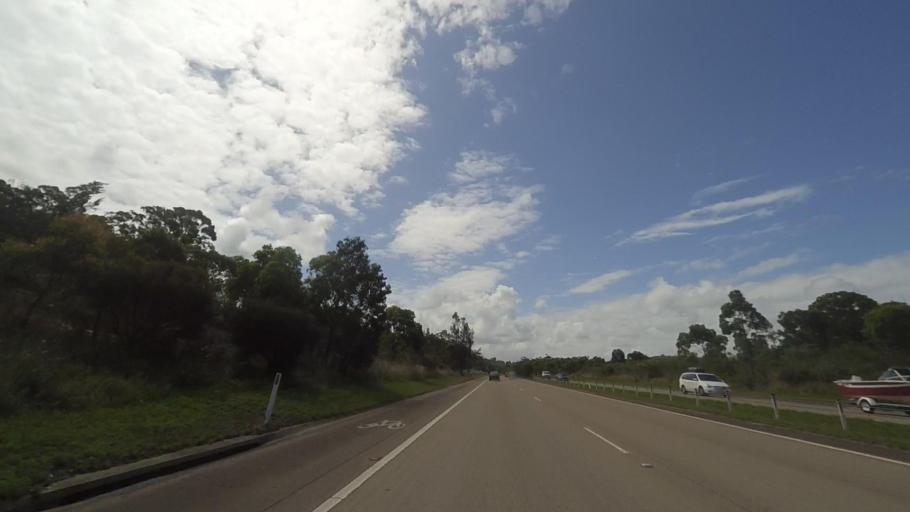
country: AU
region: New South Wales
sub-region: Lake Macquarie Shire
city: Windale
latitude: -32.9858
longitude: 151.6843
